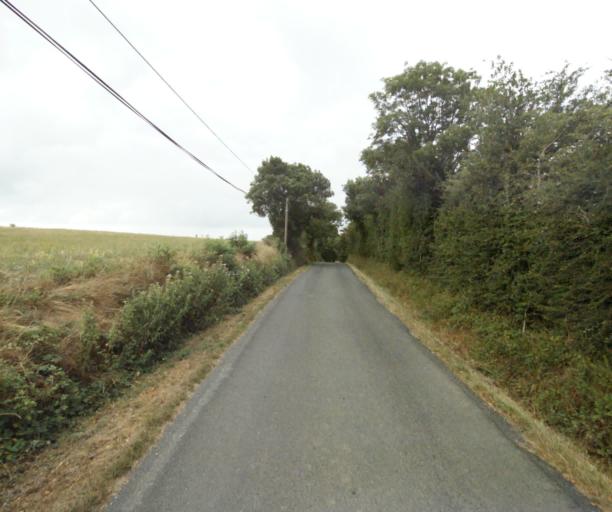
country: FR
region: Midi-Pyrenees
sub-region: Departement du Tarn
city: Soreze
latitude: 43.3978
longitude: 2.0573
